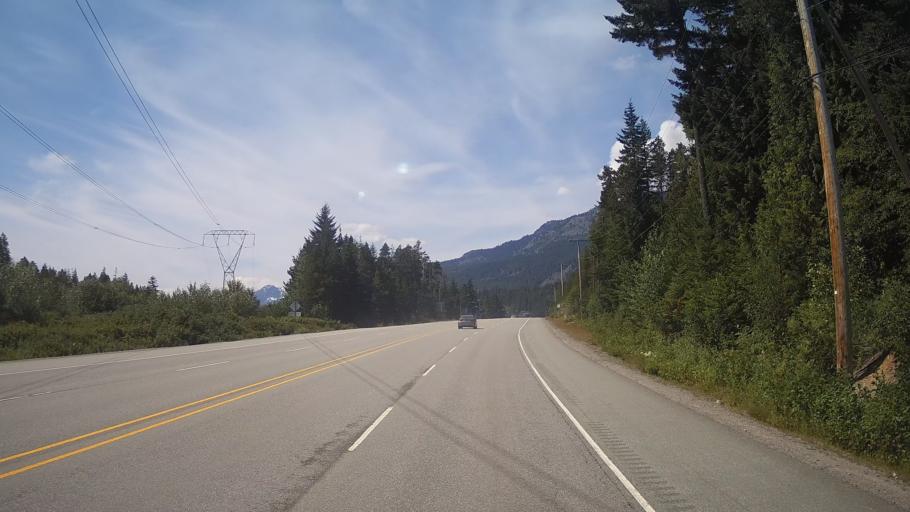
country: CA
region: British Columbia
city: Whistler
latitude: 50.0563
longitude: -123.1138
